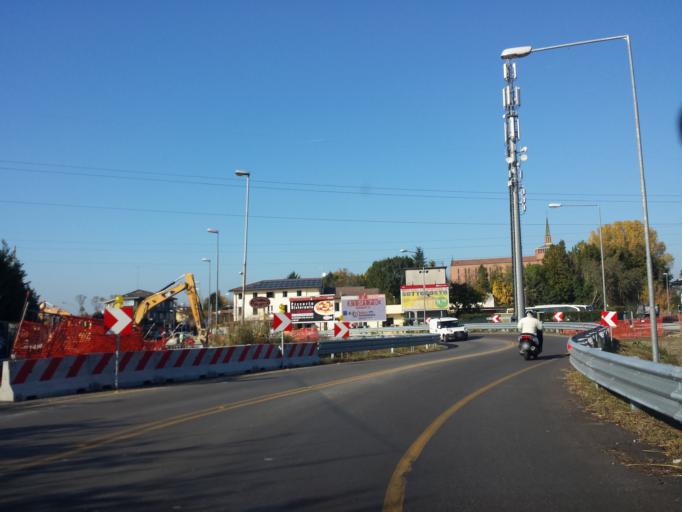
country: IT
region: Veneto
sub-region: Provincia di Padova
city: Padova
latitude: 45.4313
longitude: 11.8724
